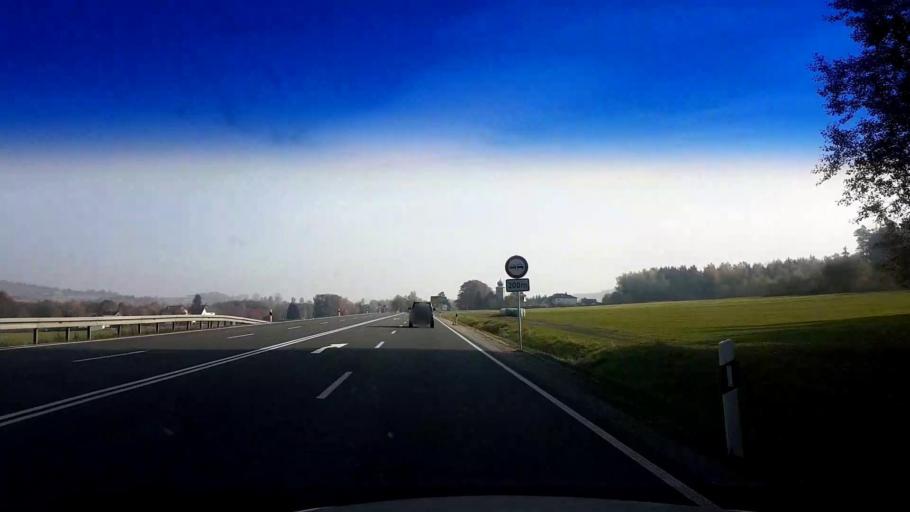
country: DE
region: Bavaria
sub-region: Upper Franconia
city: Trostau
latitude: 50.0155
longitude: 11.9298
